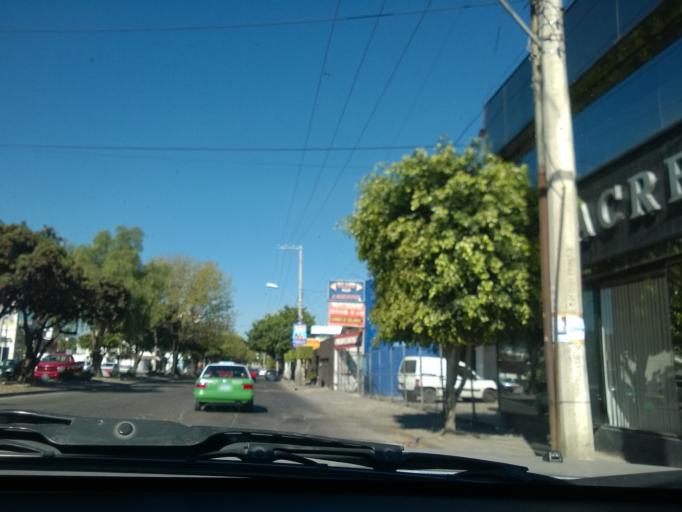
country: MX
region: Guanajuato
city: Leon
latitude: 21.1104
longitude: -101.6705
